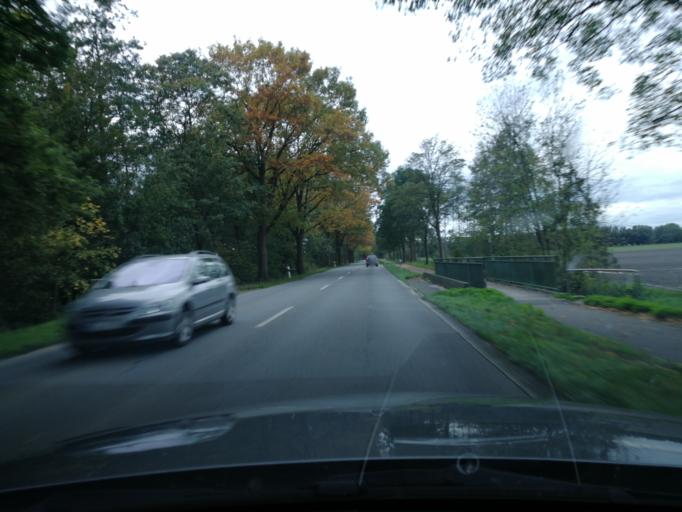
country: DE
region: North Rhine-Westphalia
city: Straelen
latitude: 51.4217
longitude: 6.2383
